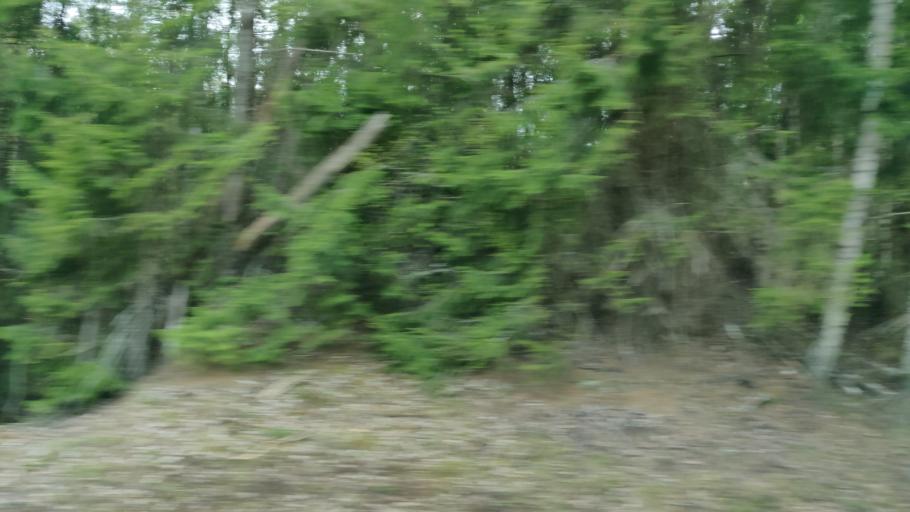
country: SE
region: Vaermland
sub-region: Forshaga Kommun
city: Deje
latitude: 59.6512
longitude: 13.4407
